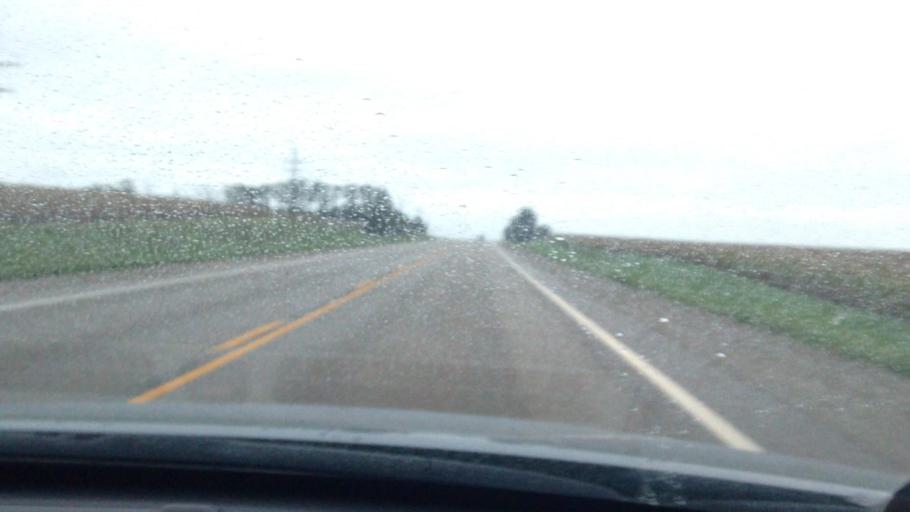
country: US
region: Kansas
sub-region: Brown County
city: Hiawatha
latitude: 39.8195
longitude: -95.5272
